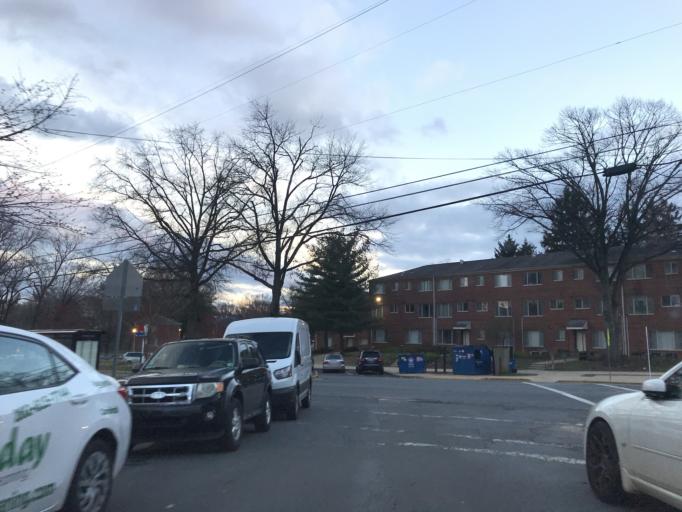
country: US
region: Maryland
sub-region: Prince George's County
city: Adelphi
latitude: 39.0083
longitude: -76.9843
